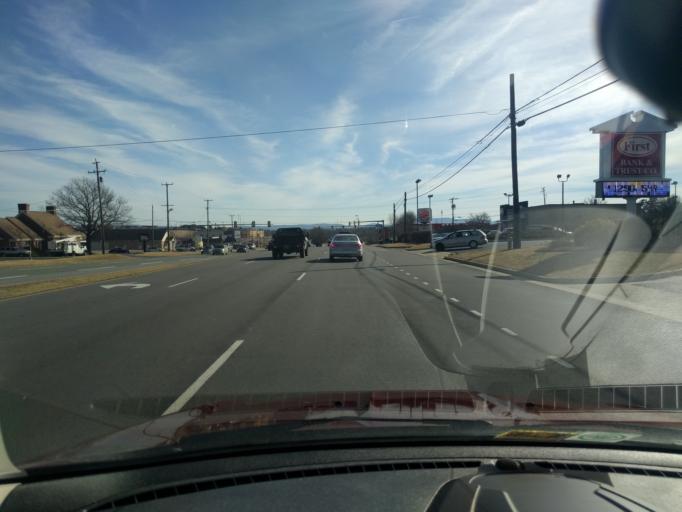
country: US
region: Virginia
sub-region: City of Staunton
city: Staunton
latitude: 38.1356
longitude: -79.0444
